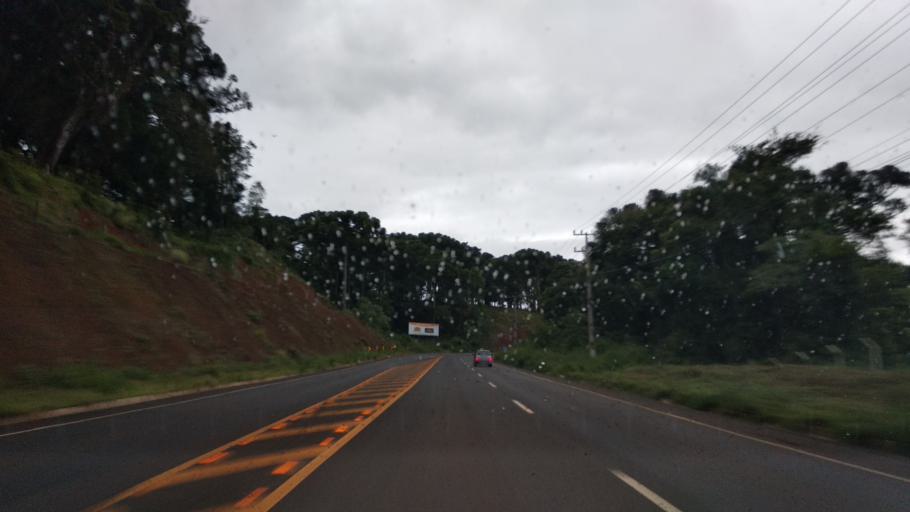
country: BR
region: Santa Catarina
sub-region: Videira
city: Videira
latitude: -27.0525
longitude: -51.1849
